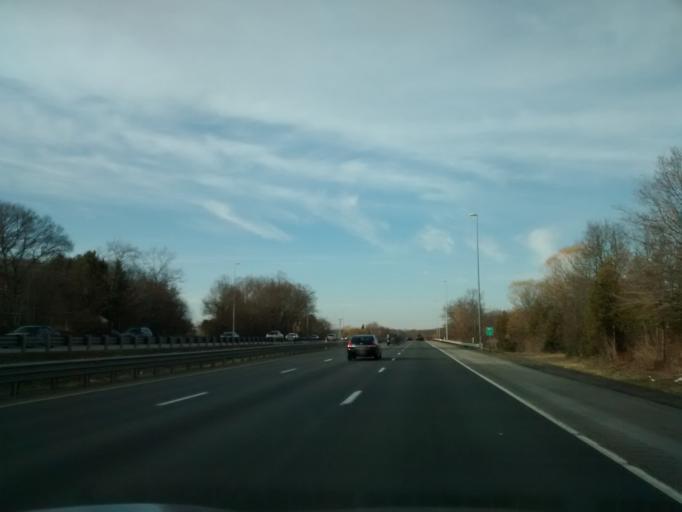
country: US
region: Massachusetts
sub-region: Worcester County
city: Auburn
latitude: 42.2067
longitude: -71.8388
